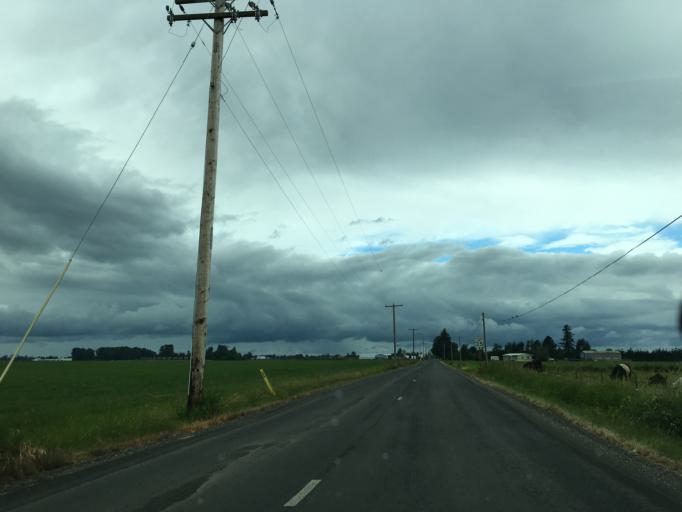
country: US
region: Washington
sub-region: Whatcom County
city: Sumas
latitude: 48.9747
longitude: -122.2593
